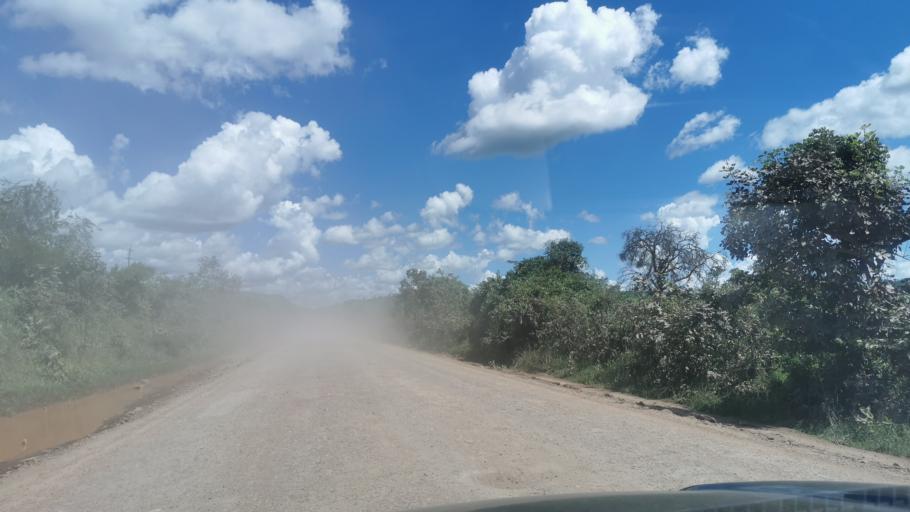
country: TZ
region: Kagera
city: Biharamulo
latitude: -2.8893
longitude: 31.1383
